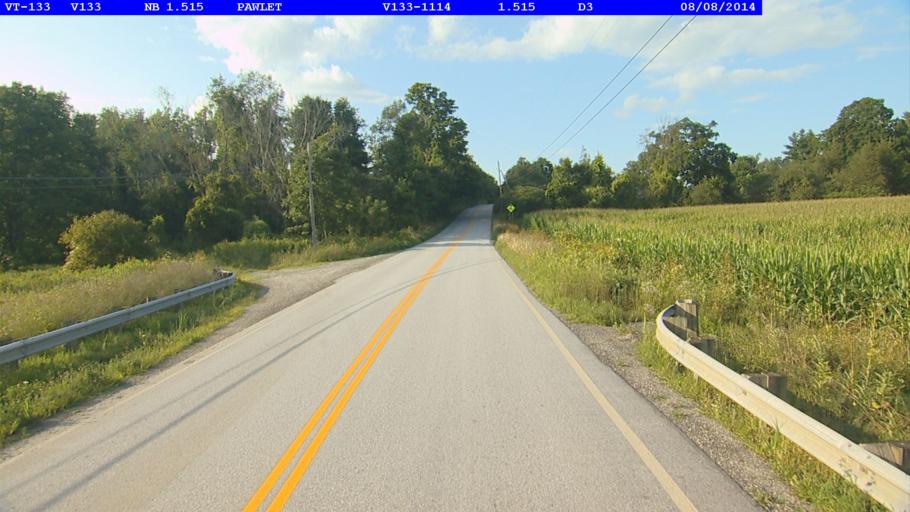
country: US
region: New York
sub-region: Washington County
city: Granville
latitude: 43.3547
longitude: -73.1528
